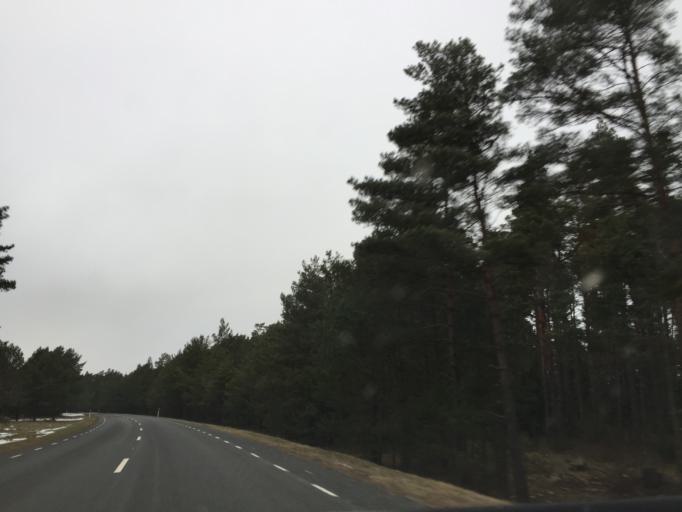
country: EE
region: Saare
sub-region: Kuressaare linn
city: Kuressaare
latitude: 58.5461
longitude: 22.3364
